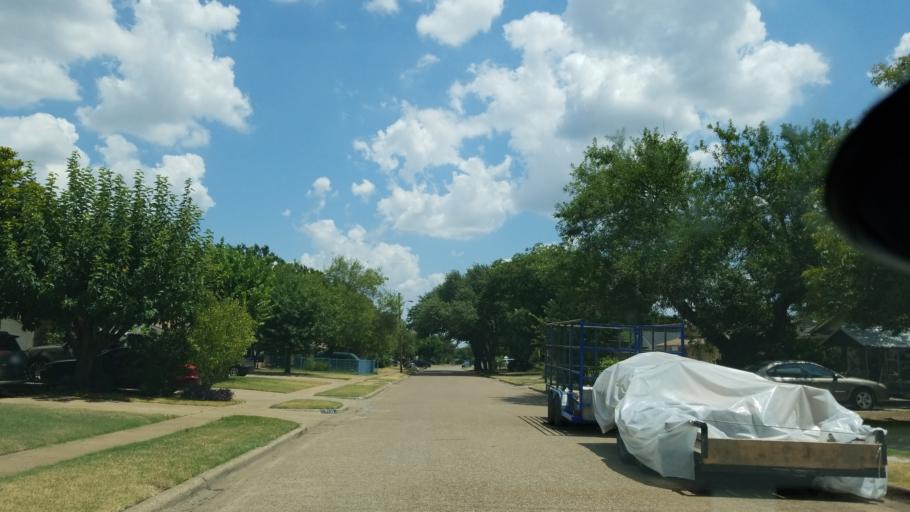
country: US
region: Texas
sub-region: Dallas County
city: Cockrell Hill
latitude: 32.7182
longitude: -96.8979
